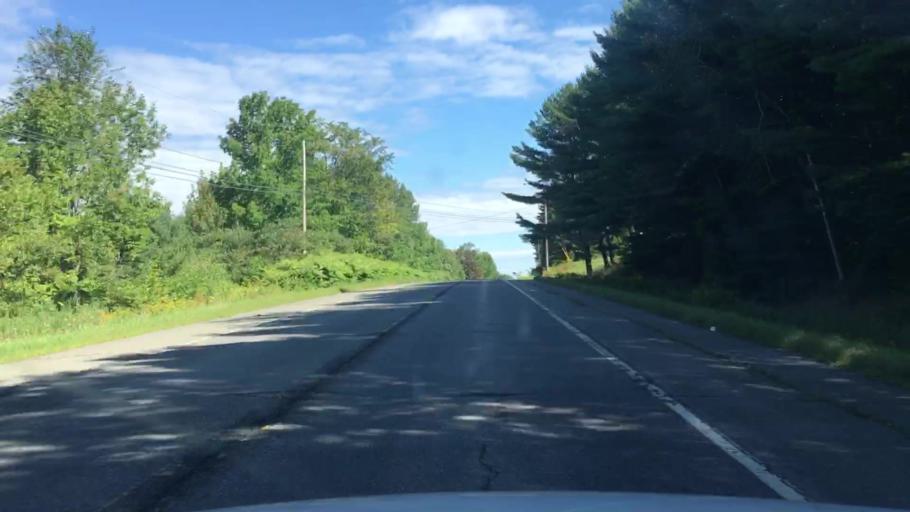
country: US
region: Maine
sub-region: Penobscot County
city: Dexter
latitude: 45.0587
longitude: -69.2523
